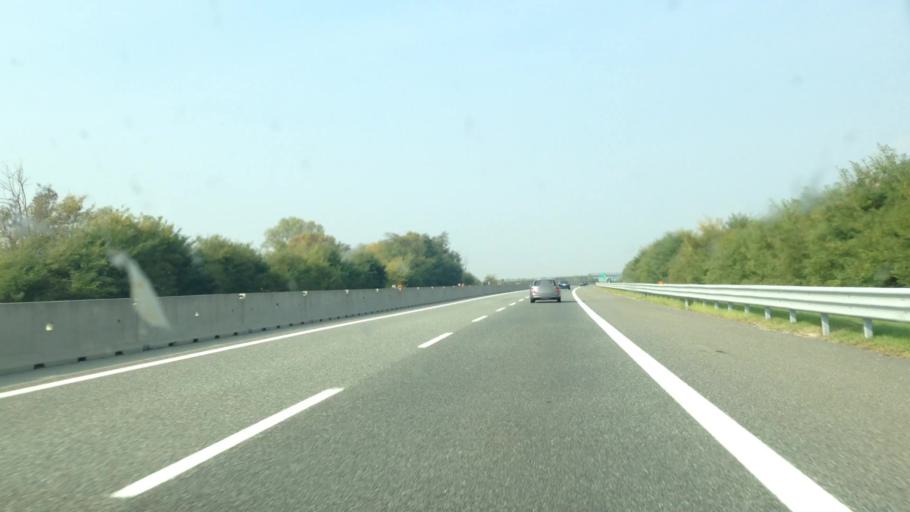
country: IT
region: Piedmont
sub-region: Provincia di Vercelli
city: Sali Vercellese
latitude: 45.3062
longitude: 8.3003
